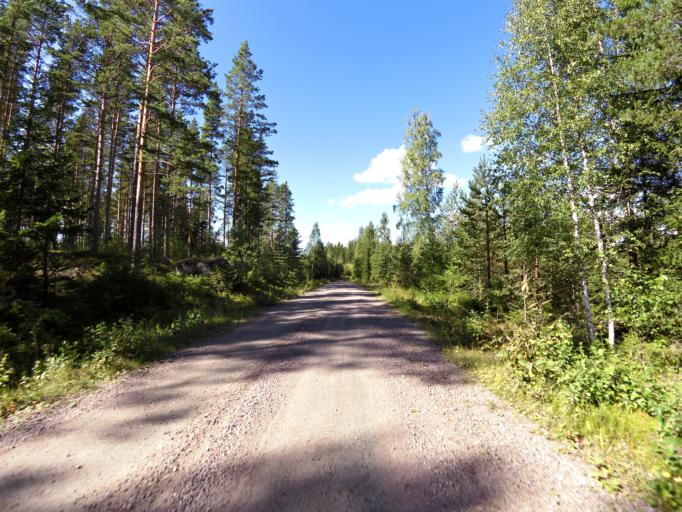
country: SE
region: Gaevleborg
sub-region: Ockelbo Kommun
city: Ockelbo
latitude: 60.7879
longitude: 16.8874
